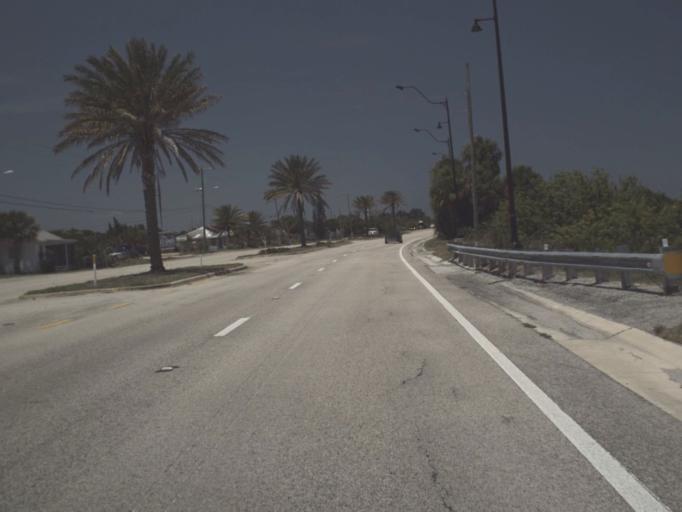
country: US
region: Florida
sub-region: Brevard County
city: Palm Bay
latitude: 28.0472
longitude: -80.5868
